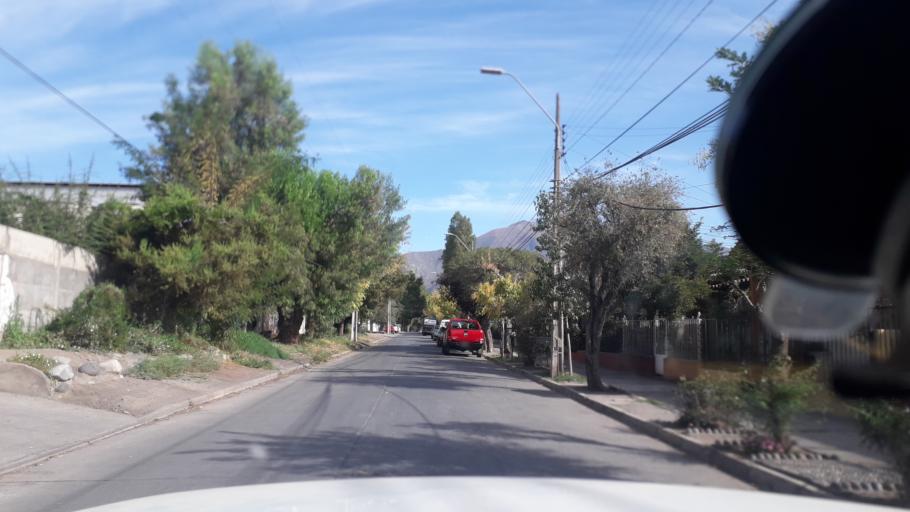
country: CL
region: Valparaiso
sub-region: Provincia de San Felipe
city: San Felipe
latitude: -32.7526
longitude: -70.7159
